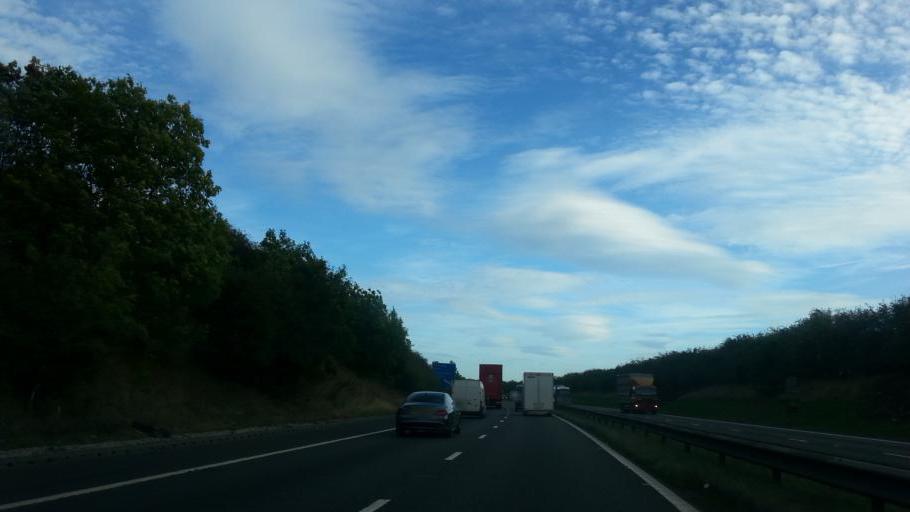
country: GB
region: England
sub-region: Doncaster
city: Bentley
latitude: 53.4960
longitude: -1.1706
